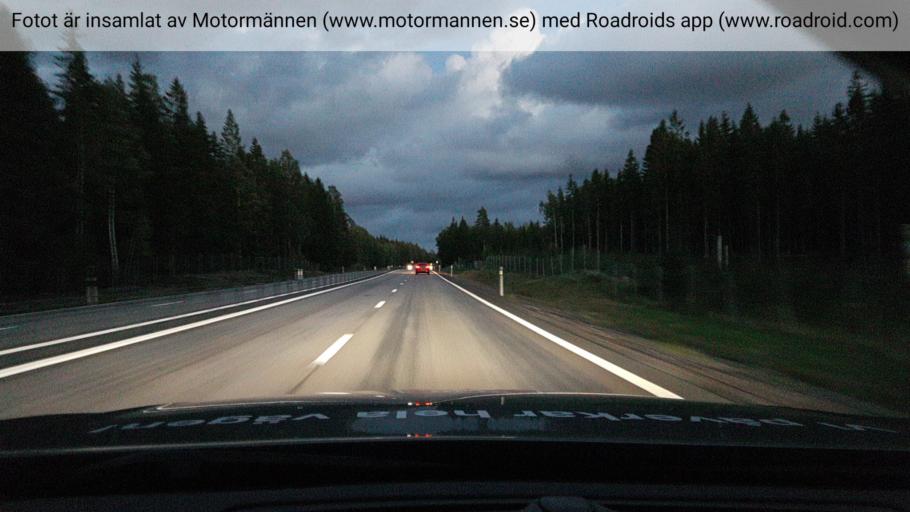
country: SE
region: Vaermland
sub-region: Kristinehamns Kommun
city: Kristinehamn
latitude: 59.3588
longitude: 14.0453
